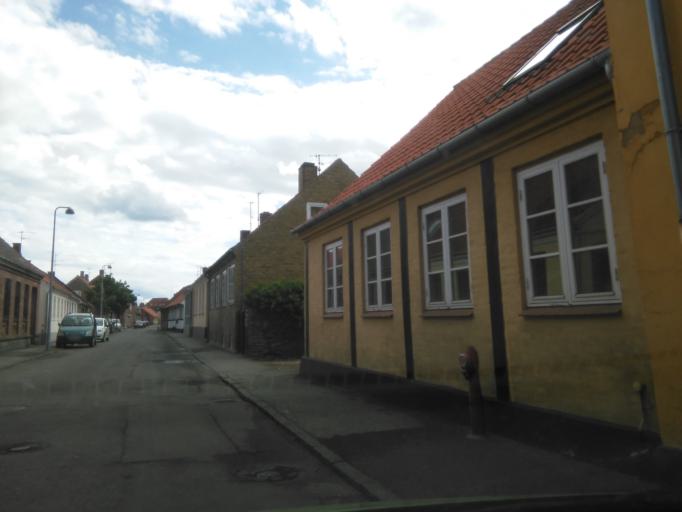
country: DK
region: Capital Region
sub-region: Bornholm Kommune
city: Nexo
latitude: 55.0660
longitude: 15.1329
